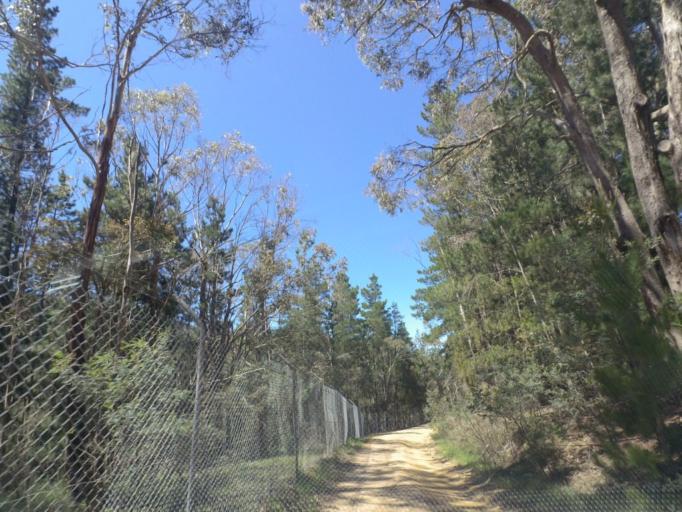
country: AU
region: Victoria
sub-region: Hume
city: Sunbury
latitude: -37.3946
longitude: 144.5559
